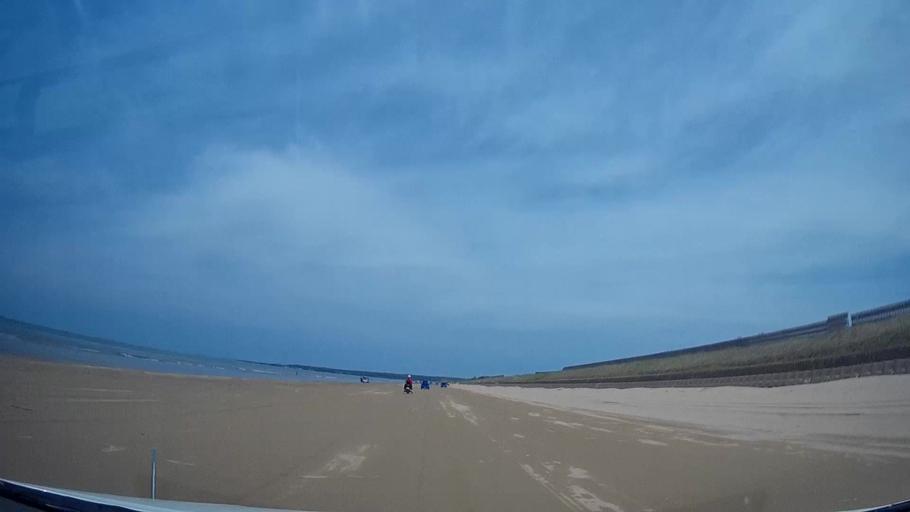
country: JP
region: Ishikawa
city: Hakui
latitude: 36.8761
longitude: 136.7613
